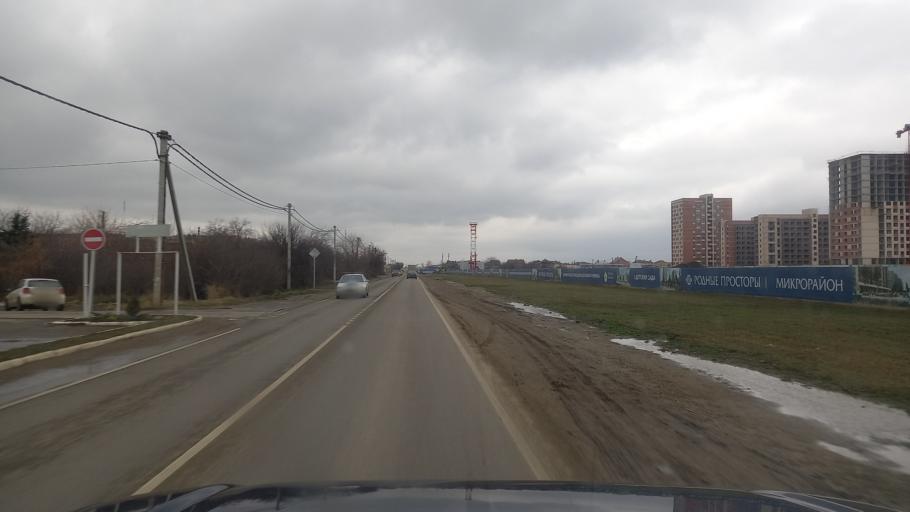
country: RU
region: Krasnodarskiy
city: Pashkovskiy
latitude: 45.0591
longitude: 39.1481
